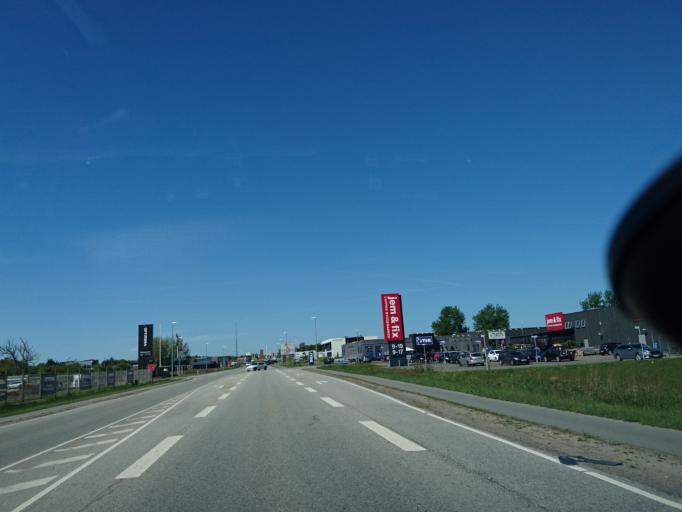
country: DK
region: North Denmark
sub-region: Hjorring Kommune
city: Hjorring
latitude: 57.4560
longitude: 10.0246
